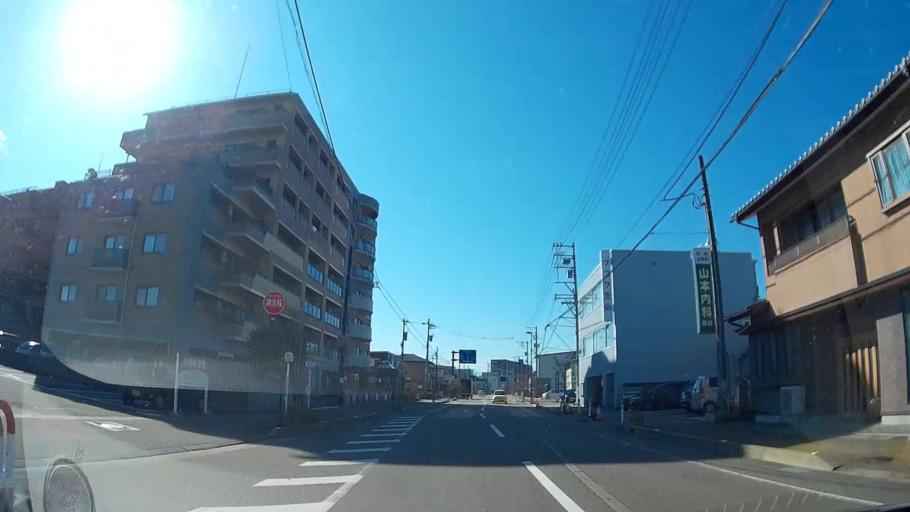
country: JP
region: Toyama
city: Nanto-shi
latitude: 36.6415
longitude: 136.9567
